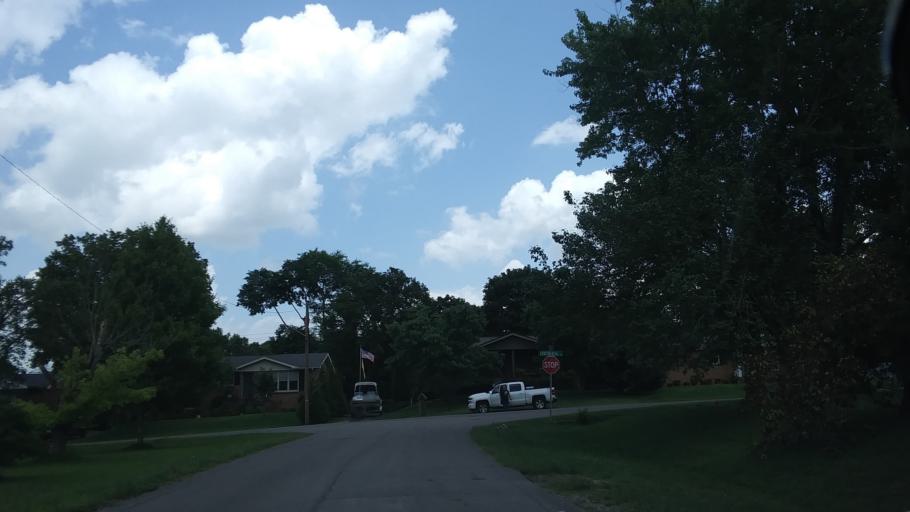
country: US
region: Tennessee
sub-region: Davidson County
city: Belle Meade
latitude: 36.1453
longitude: -86.8869
